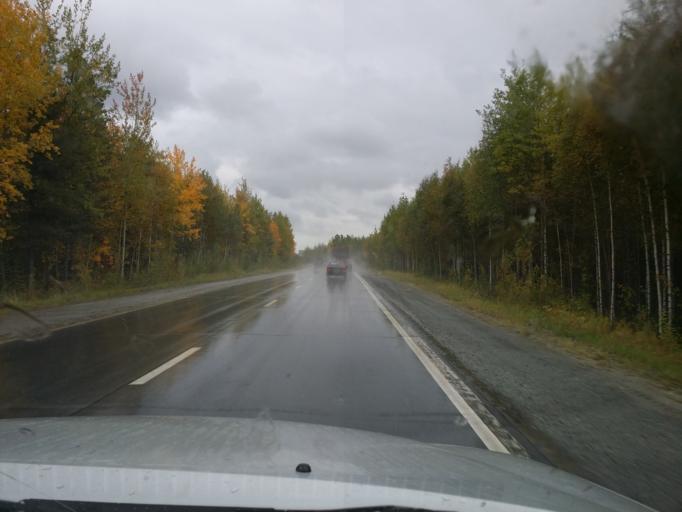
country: RU
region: Khanty-Mansiyskiy Avtonomnyy Okrug
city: Megion
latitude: 61.1292
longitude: 75.7865
